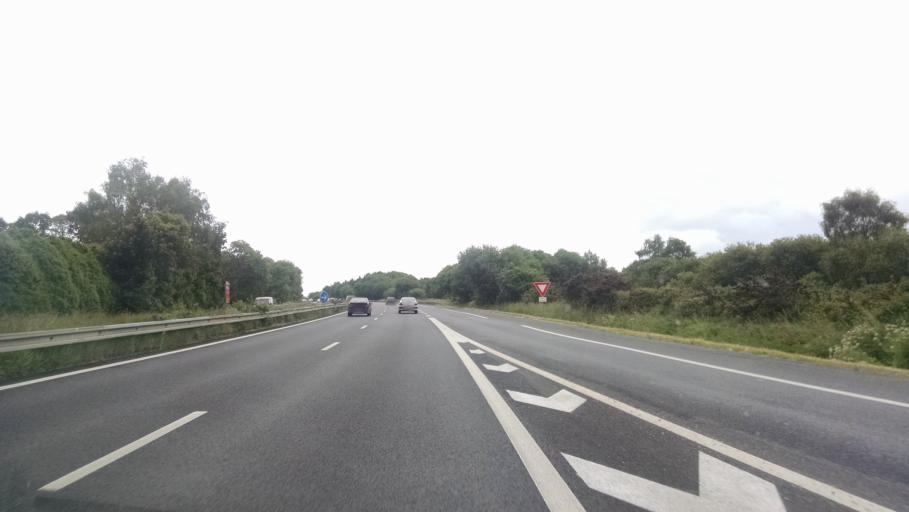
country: FR
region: Brittany
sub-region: Departement du Morbihan
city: Queven
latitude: 47.7781
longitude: -3.4161
